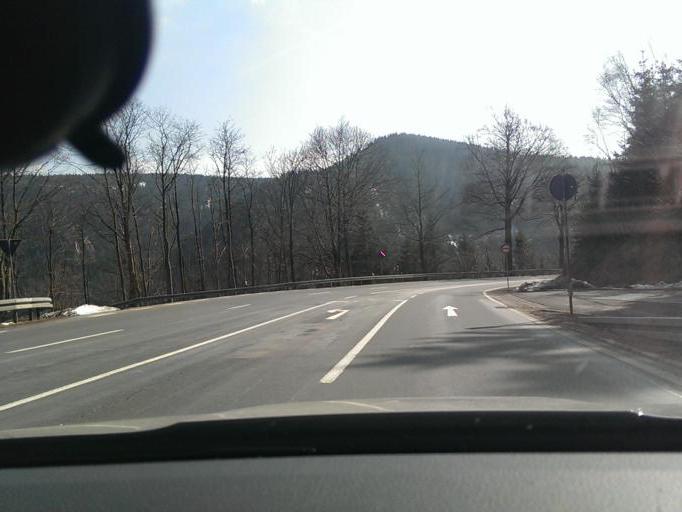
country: DE
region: Thuringia
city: Oberhof
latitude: 50.6837
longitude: 10.7003
